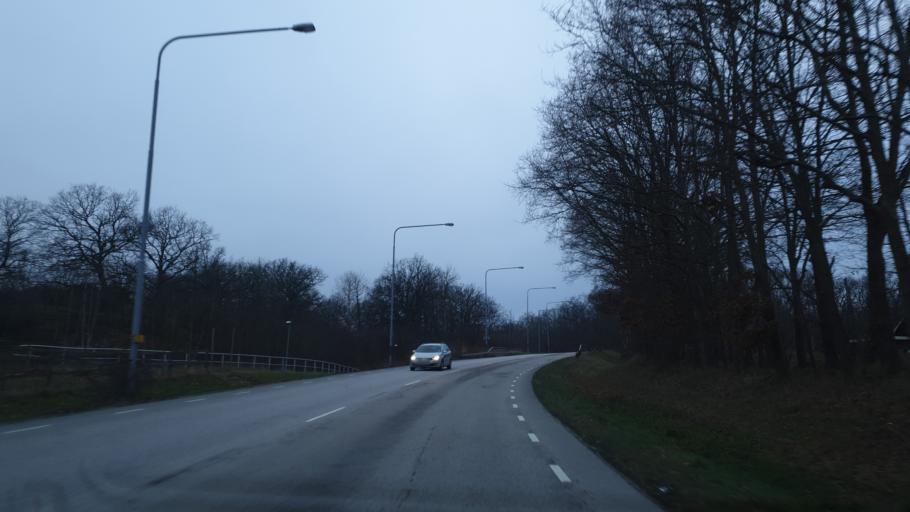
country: SE
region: Blekinge
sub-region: Karlskrona Kommun
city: Rodeby
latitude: 56.2074
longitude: 15.6532
